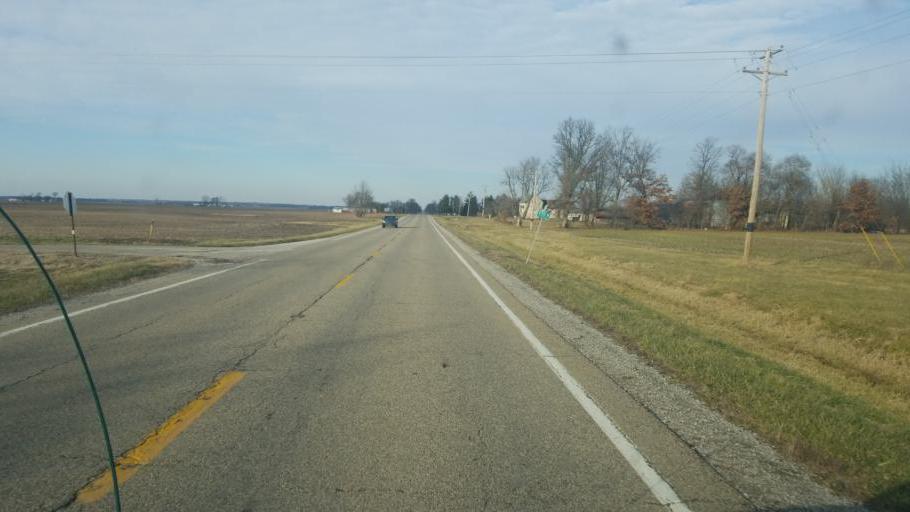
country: US
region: Illinois
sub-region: Lawrence County
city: Bridgeport
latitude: 38.5753
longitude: -87.6945
